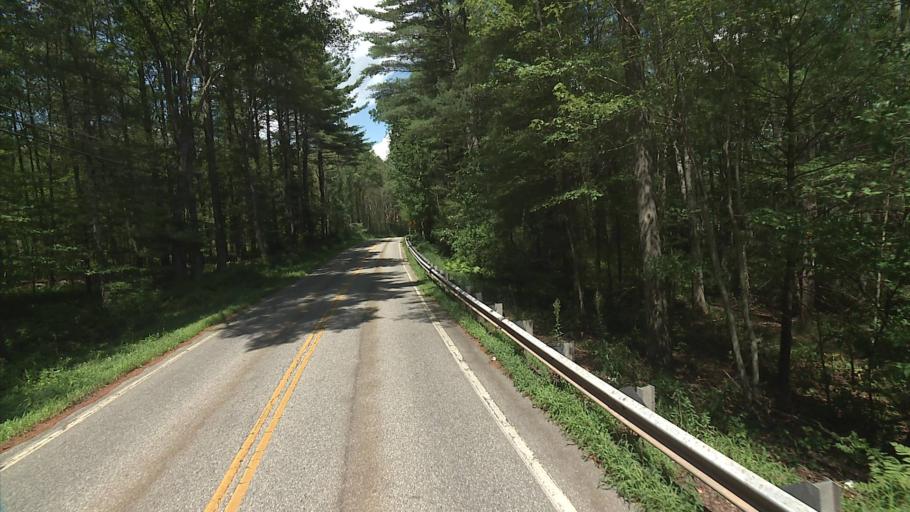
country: US
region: Connecticut
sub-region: Tolland County
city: Mansfield City
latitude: 41.8064
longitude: -72.1709
